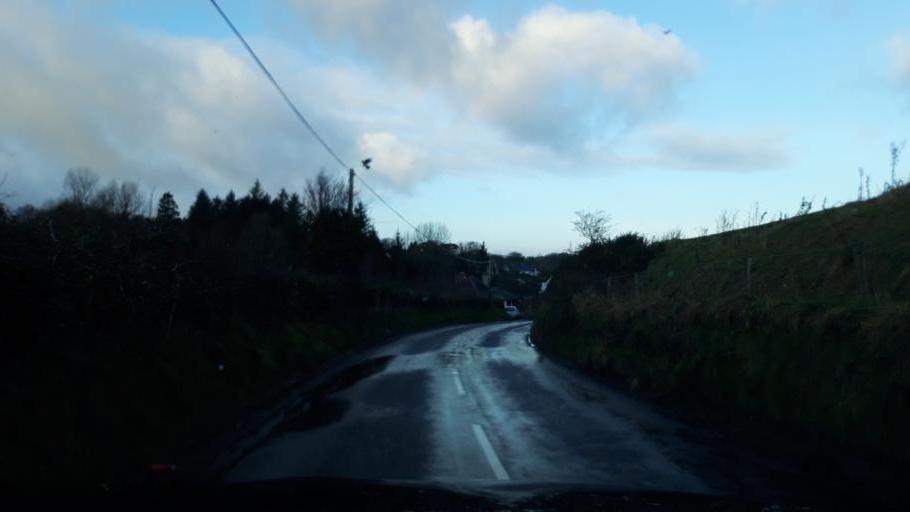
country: GB
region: Northern Ireland
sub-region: Moyle District
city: Ballycastle
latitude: 55.1980
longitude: -6.2300
